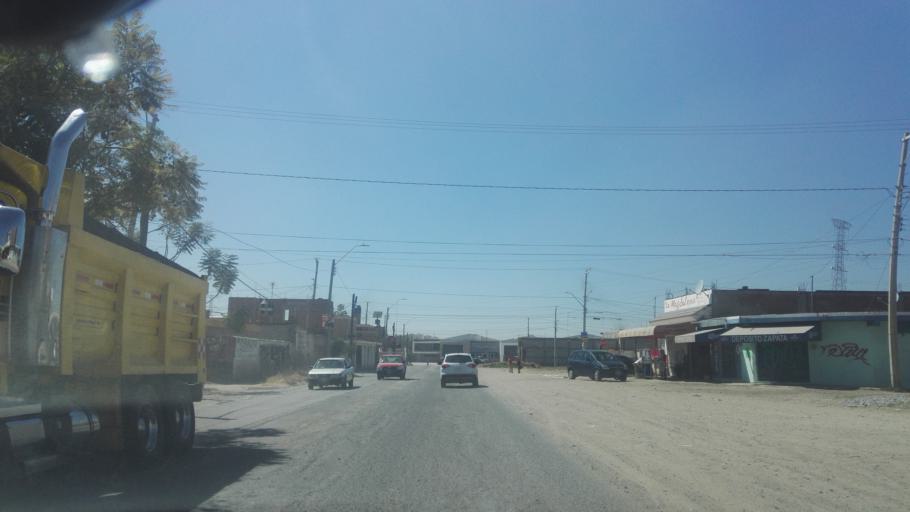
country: MX
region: Guanajuato
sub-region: Leon
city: Fraccionamiento Paraiso Real
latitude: 21.0912
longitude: -101.5935
